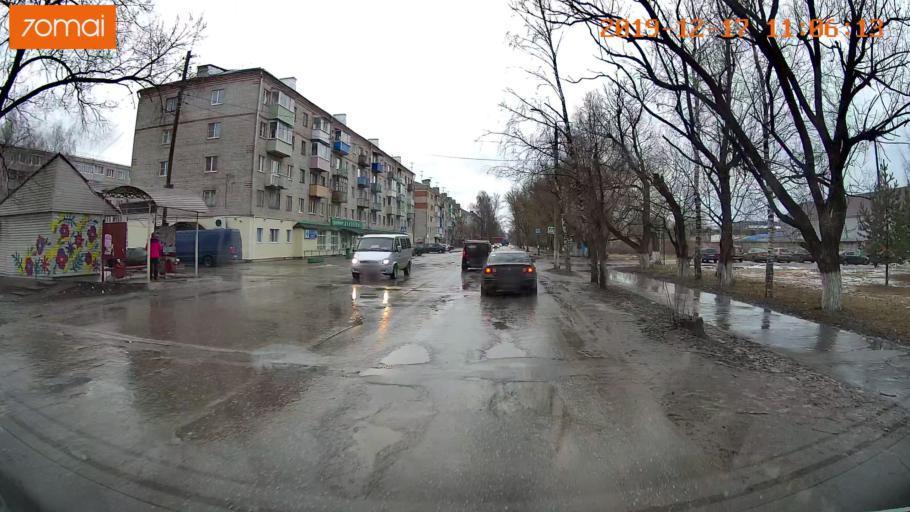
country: RU
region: Vladimir
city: Gus'-Khrustal'nyy
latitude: 55.6166
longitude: 40.6446
